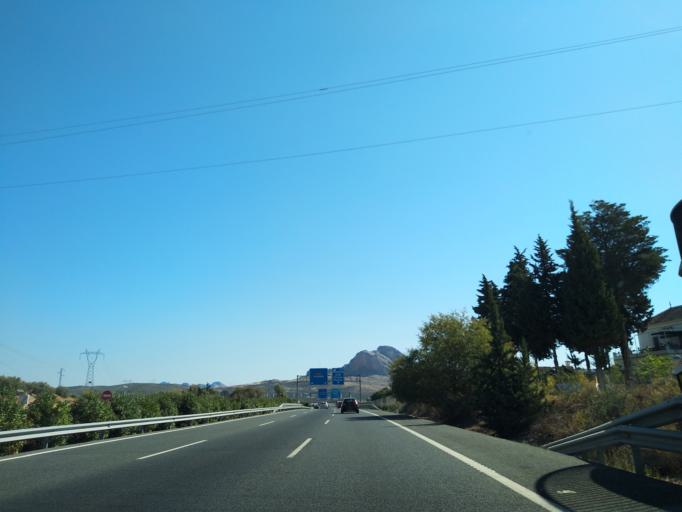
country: ES
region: Andalusia
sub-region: Provincia de Malaga
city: Antequera
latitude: 37.0700
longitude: -4.5386
